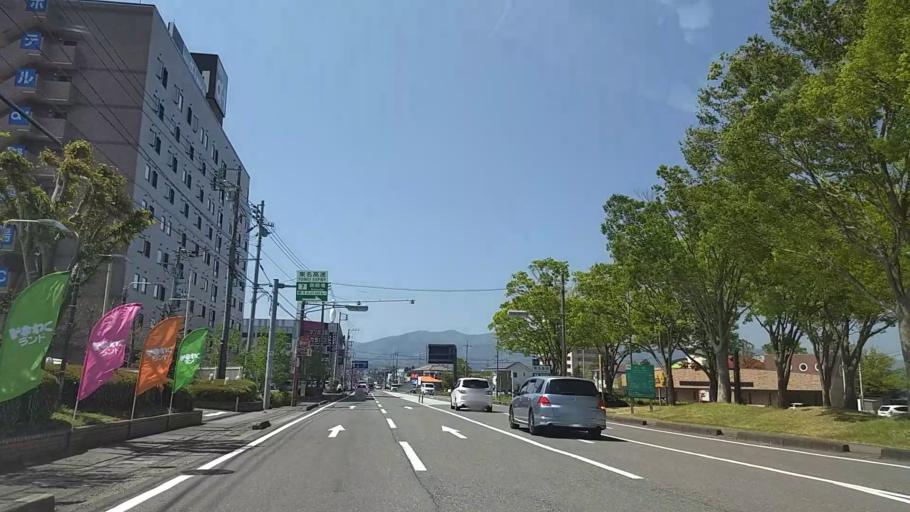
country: JP
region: Shizuoka
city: Gotemba
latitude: 35.2944
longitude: 138.9452
